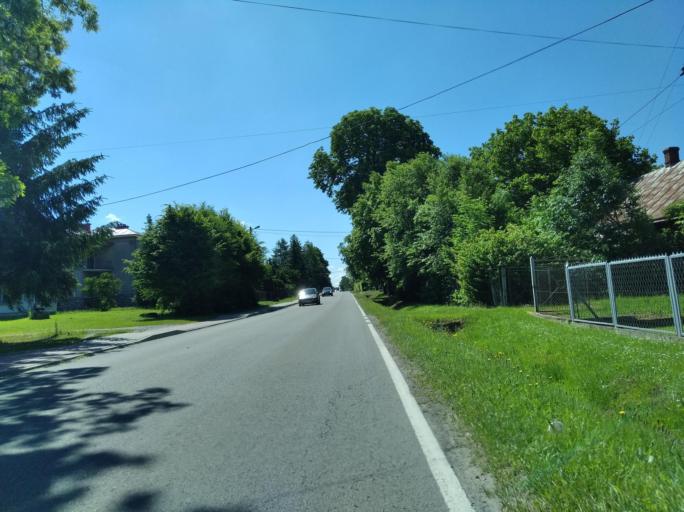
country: PL
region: Subcarpathian Voivodeship
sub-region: Powiat krosnienski
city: Chorkowka
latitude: 49.6617
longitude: 21.6930
